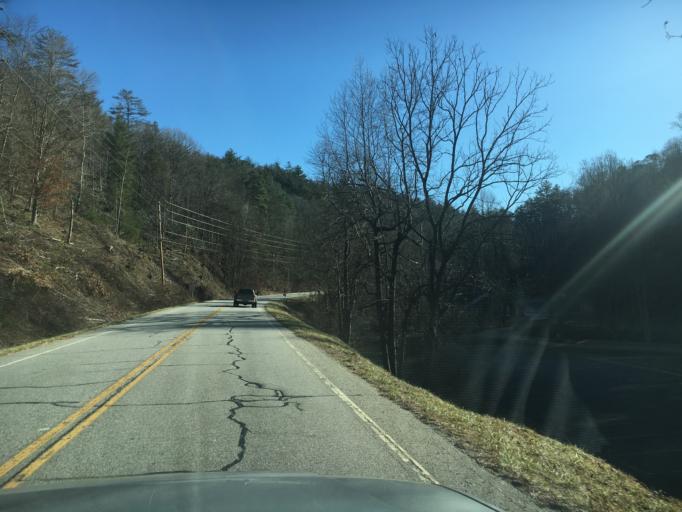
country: US
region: Georgia
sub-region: Union County
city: Blairsville
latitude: 34.7802
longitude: -83.9093
